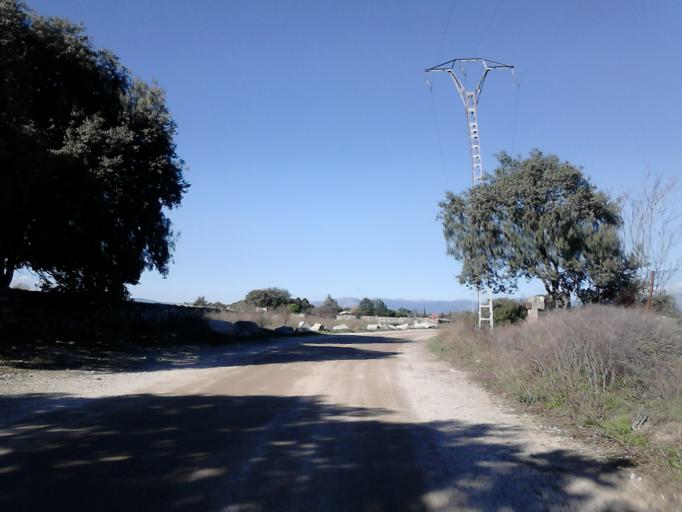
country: ES
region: Madrid
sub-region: Provincia de Madrid
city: Galapagar
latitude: 40.5642
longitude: -3.9954
